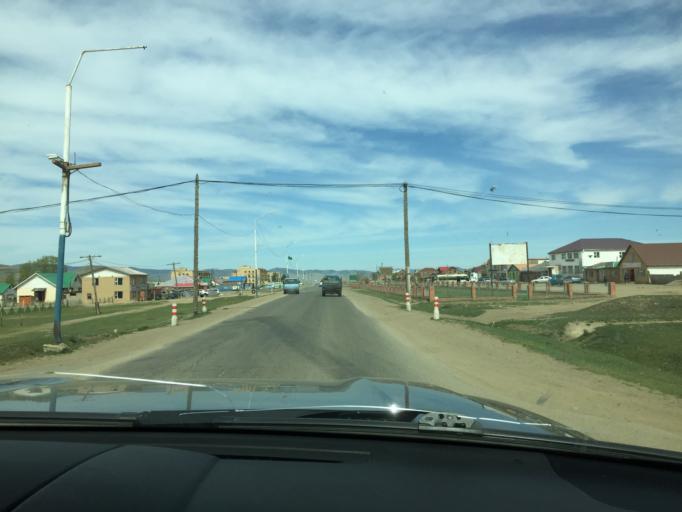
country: MN
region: Central Aimak
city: Ihsueuej
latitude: 48.2235
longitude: 106.2949
